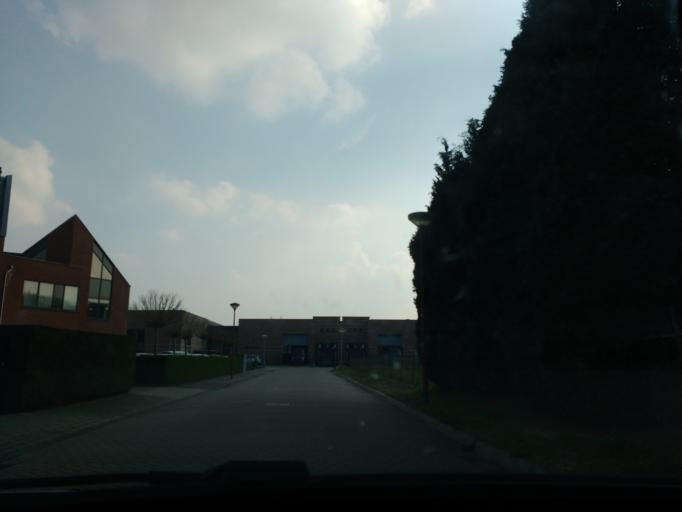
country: NL
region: Utrecht
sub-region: Gemeente Nieuwegein
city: Nieuwegein
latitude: 52.0361
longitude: 5.1020
